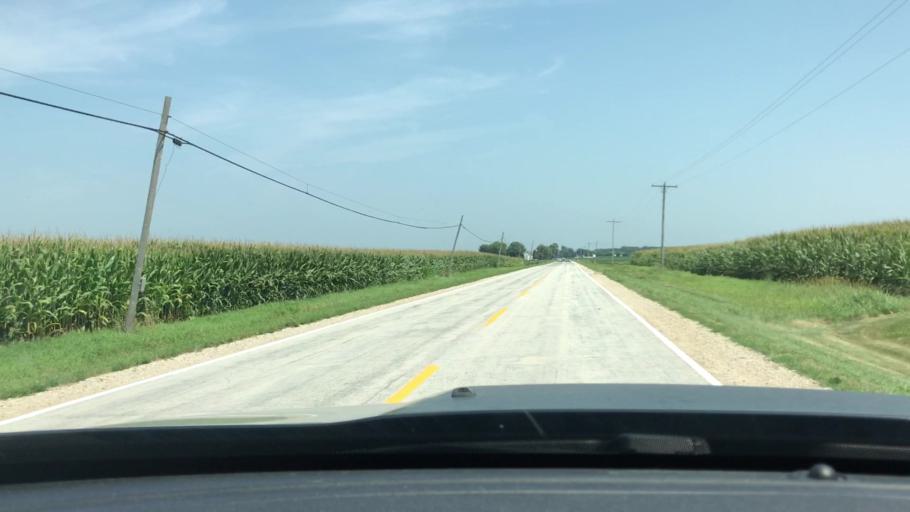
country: US
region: Illinois
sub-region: LaSalle County
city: Sheridan
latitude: 41.5047
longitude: -88.7300
